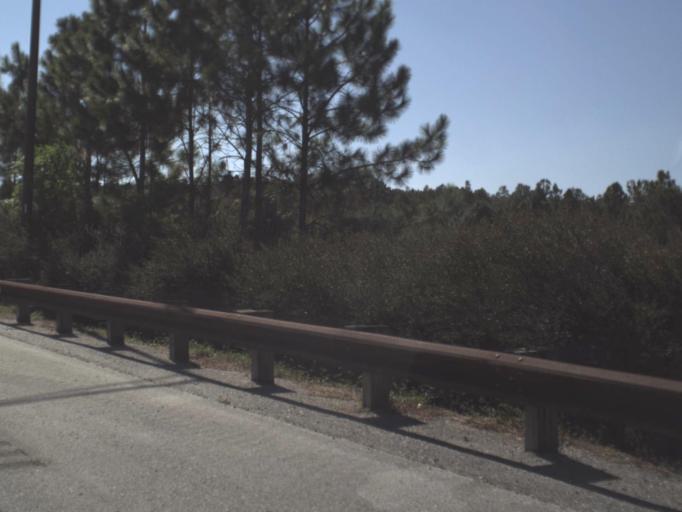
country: US
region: Florida
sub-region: Hillsborough County
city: Greater Northdale
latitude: 28.1283
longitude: -82.5484
